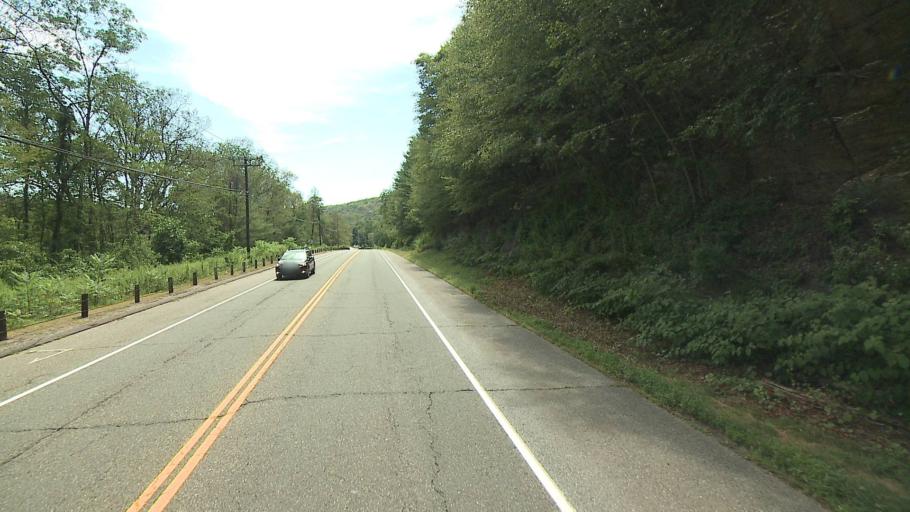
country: US
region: Connecticut
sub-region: Hartford County
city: Collinsville
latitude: 41.7865
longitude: -72.9248
